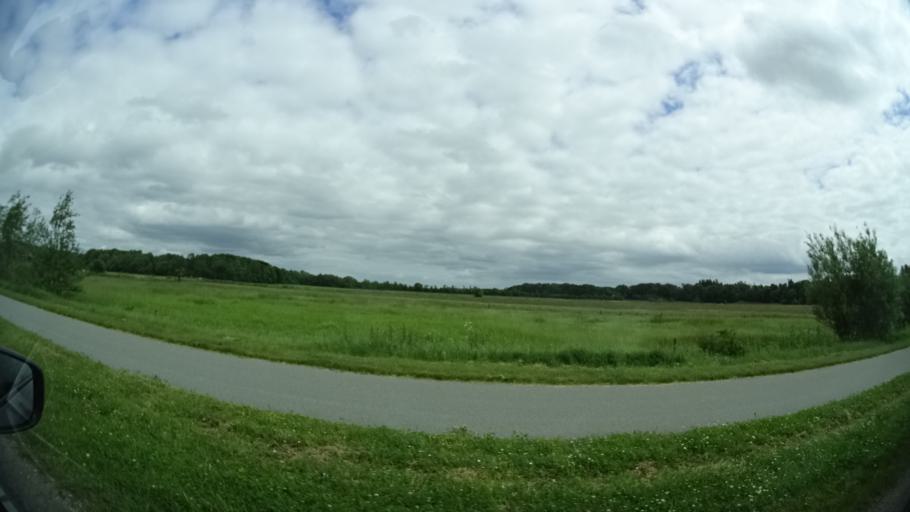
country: DK
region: Central Jutland
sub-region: Syddjurs Kommune
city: Ryomgard
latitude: 56.3768
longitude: 10.5024
